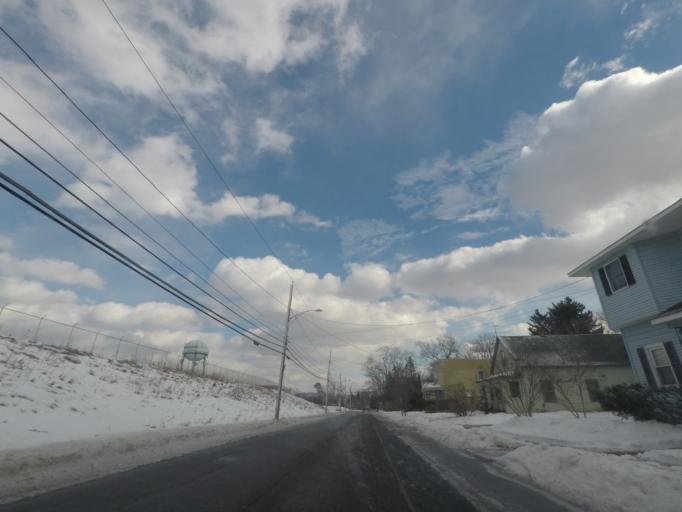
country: US
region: New York
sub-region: Albany County
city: Cohoes
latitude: 42.7792
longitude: -73.7250
